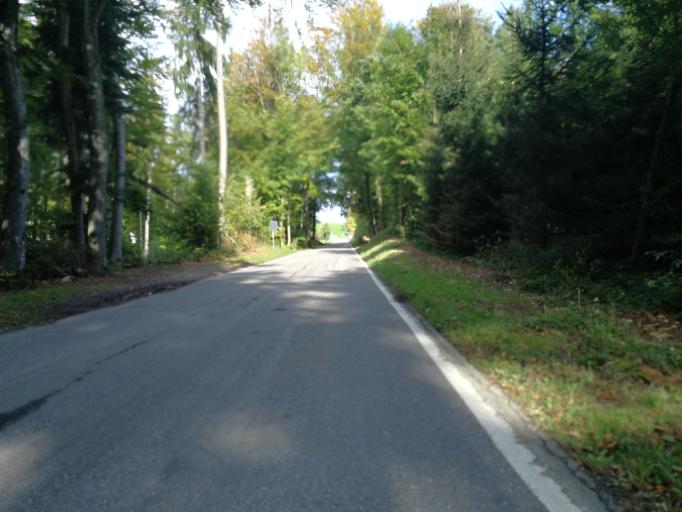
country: CH
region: Zurich
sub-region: Bezirk Uster
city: Egg
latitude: 47.2840
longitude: 8.6838
